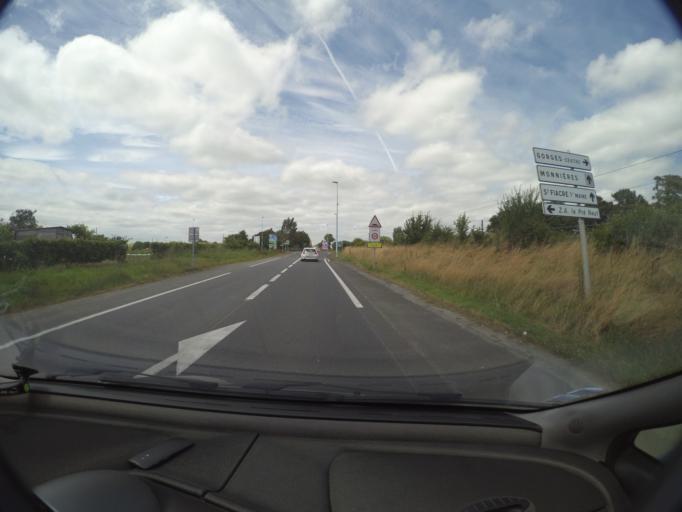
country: FR
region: Pays de la Loire
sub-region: Departement de la Loire-Atlantique
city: Gorges
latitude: 47.0990
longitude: -1.3048
